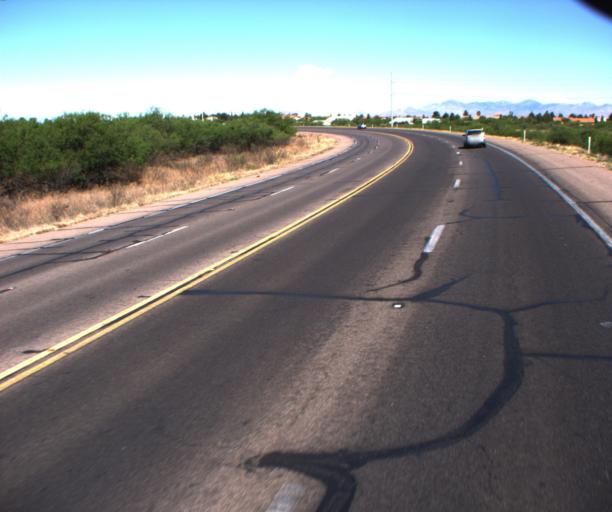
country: US
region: Arizona
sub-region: Cochise County
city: Sierra Vista
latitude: 31.5676
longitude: -110.2579
